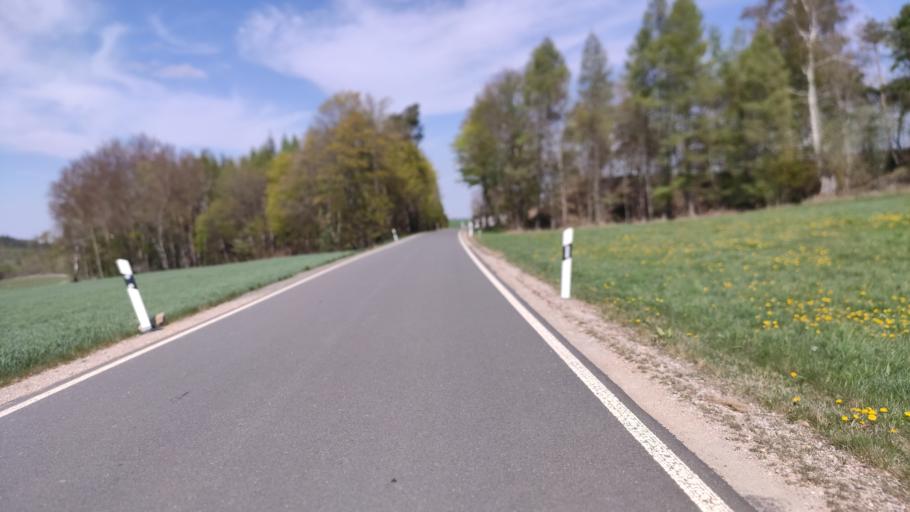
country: DE
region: Bavaria
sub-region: Upper Franconia
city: Ludwigsstadt
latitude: 50.4888
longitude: 11.4597
